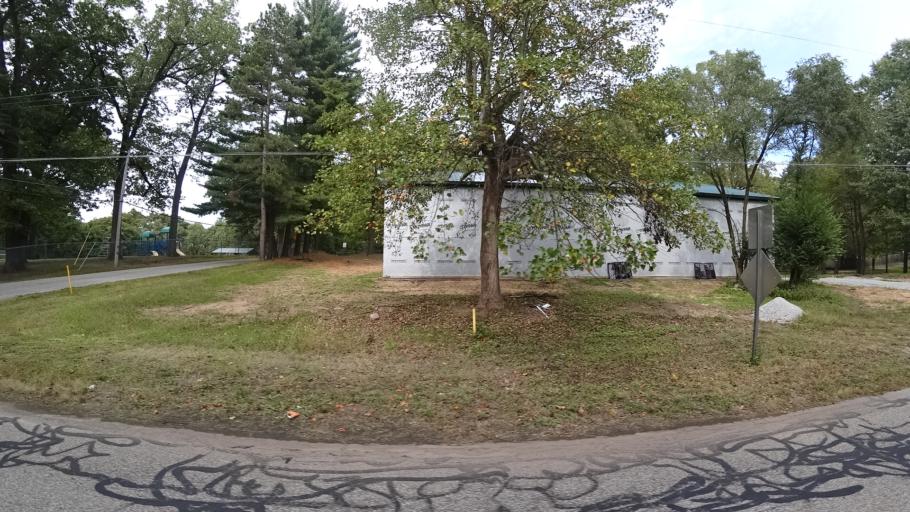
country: US
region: Indiana
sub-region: LaPorte County
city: Long Beach
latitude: 41.7277
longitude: -86.8577
